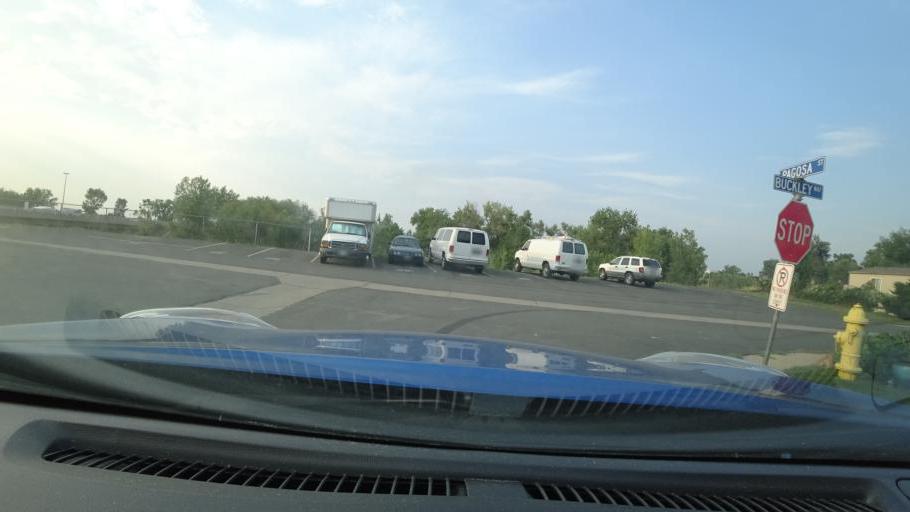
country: US
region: Colorado
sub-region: Adams County
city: Aurora
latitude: 39.7471
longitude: -104.7903
